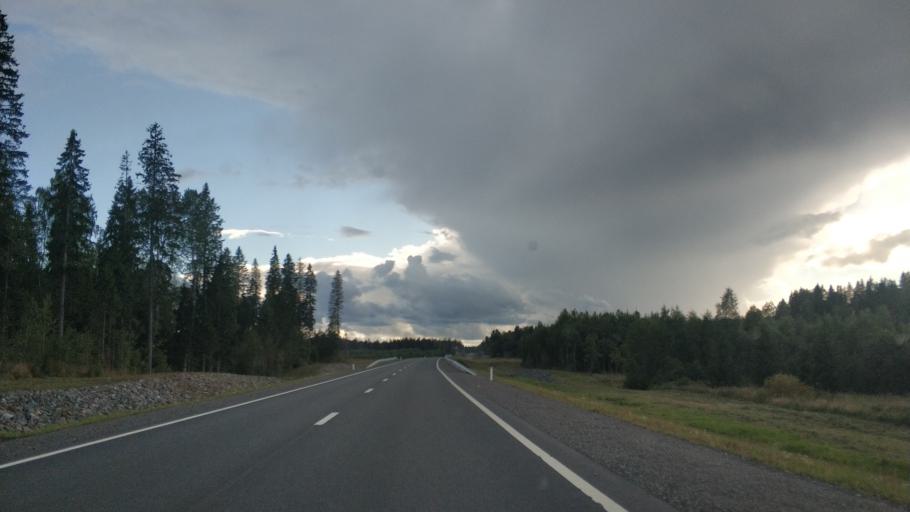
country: RU
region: Republic of Karelia
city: Lakhdenpokh'ya
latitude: 61.4483
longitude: 29.9934
